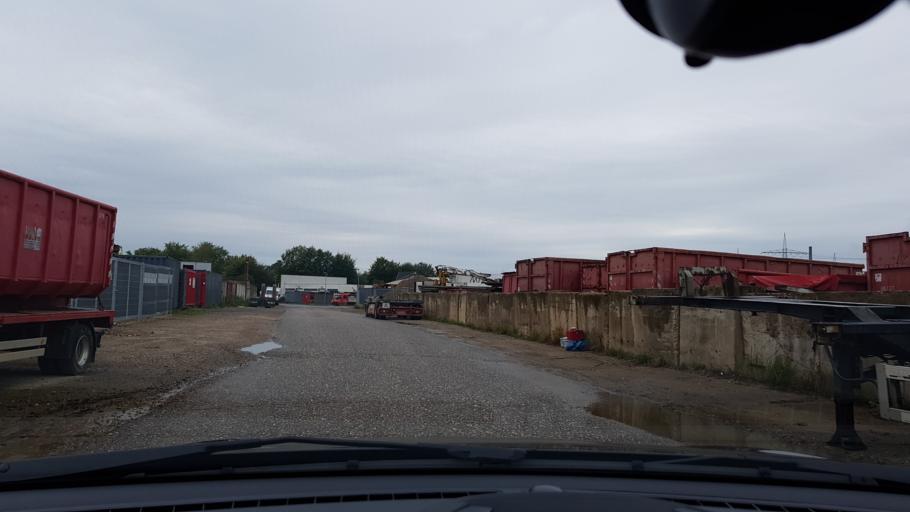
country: DE
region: North Rhine-Westphalia
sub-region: Regierungsbezirk Dusseldorf
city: Rommerskirchen
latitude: 50.9926
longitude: 6.6812
